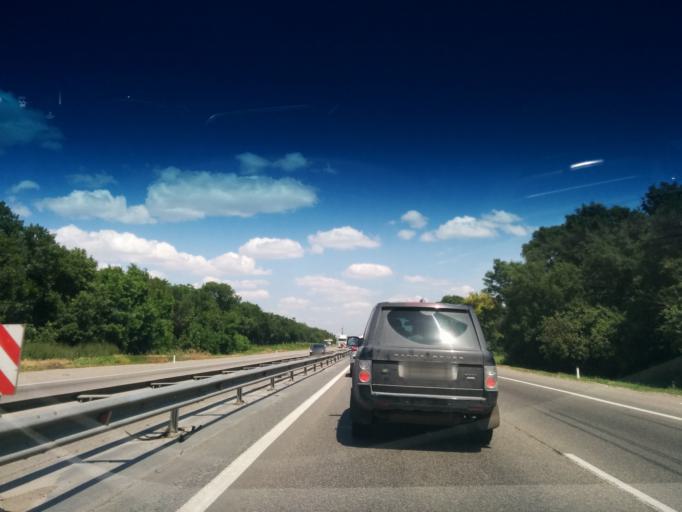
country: RU
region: Rostov
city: Grushevskaya
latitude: 47.3867
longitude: 39.9124
